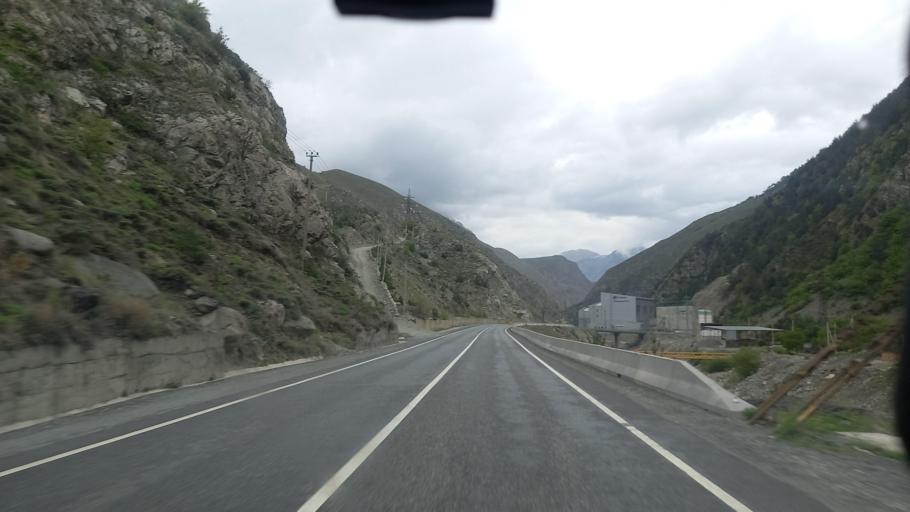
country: RU
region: North Ossetia
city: Mizur
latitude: 42.8434
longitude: 44.0363
